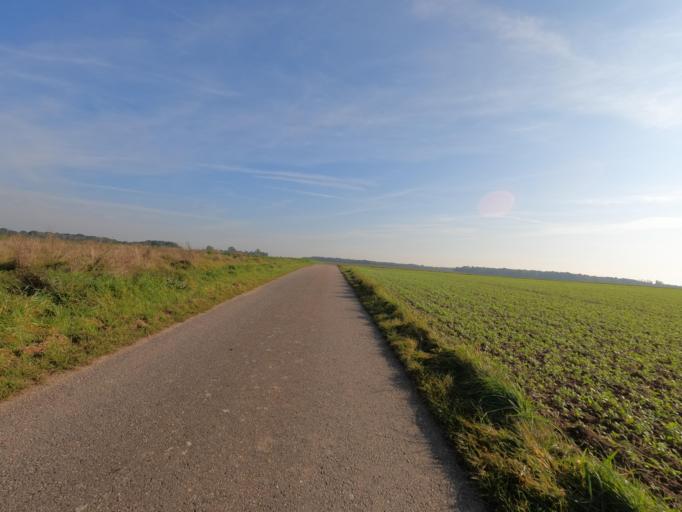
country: DE
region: North Rhine-Westphalia
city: Huckelhoven
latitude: 51.0436
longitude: 6.2600
